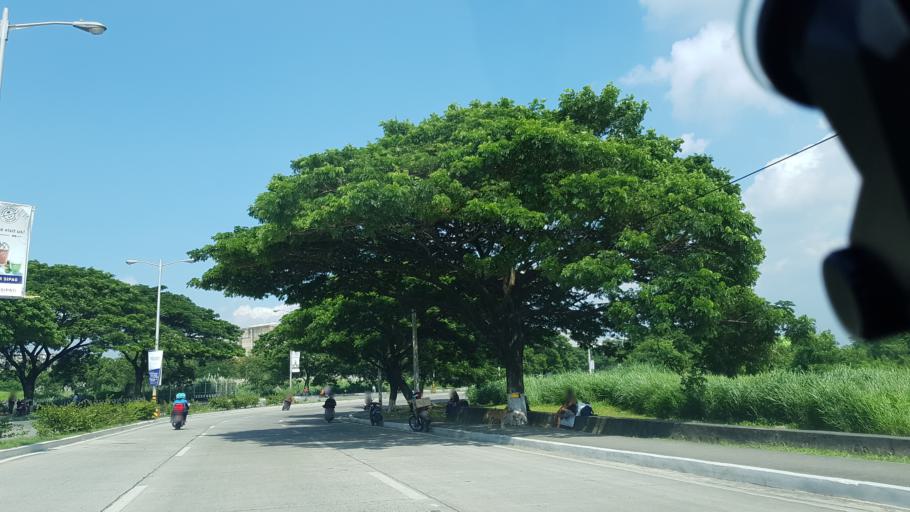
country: PH
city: Sambayanihan People's Village
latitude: 14.4832
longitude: 120.9893
